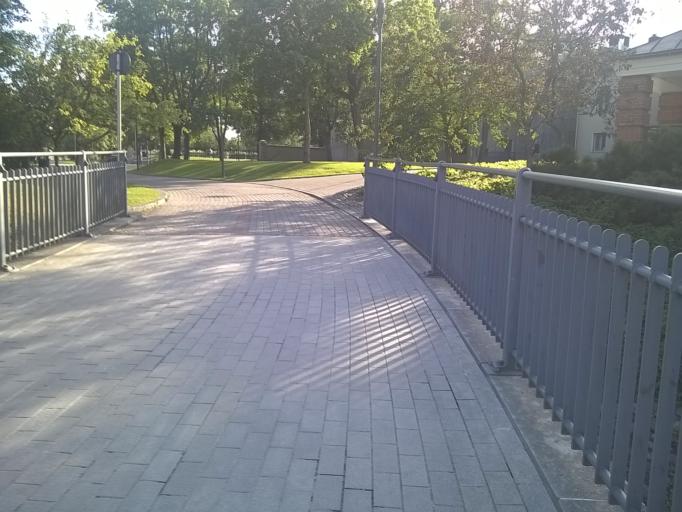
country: FI
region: Pirkanmaa
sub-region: Tampere
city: Tampere
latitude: 61.5003
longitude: 23.7618
